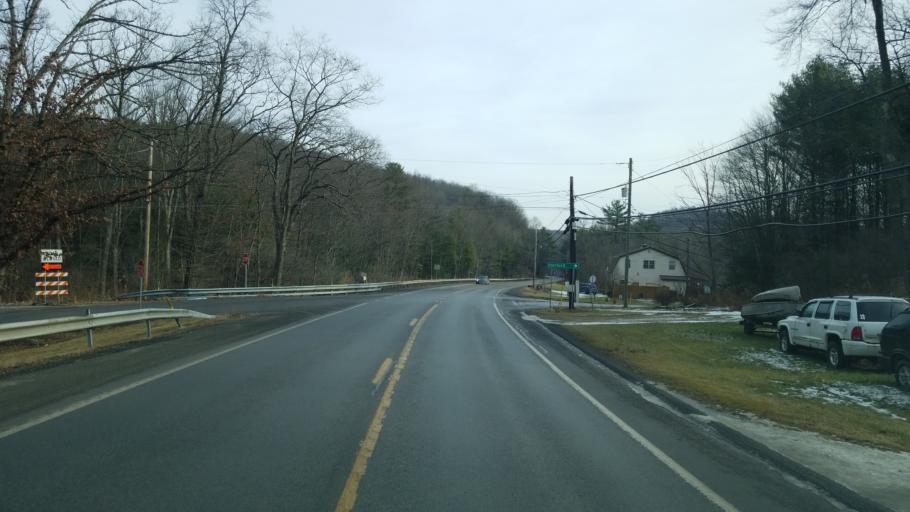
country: US
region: Pennsylvania
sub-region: Indiana County
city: Clymer
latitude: 40.7088
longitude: -78.9626
